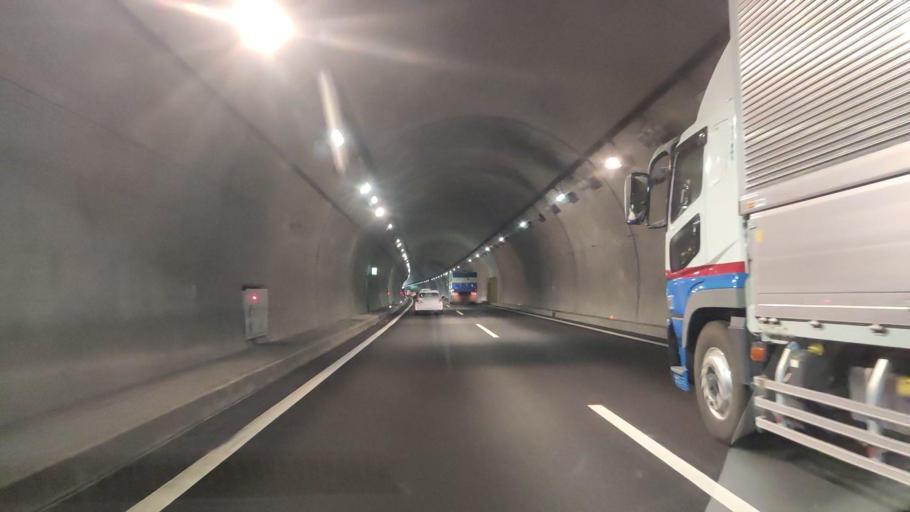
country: JP
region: Kanagawa
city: Zama
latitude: 35.5139
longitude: 139.3613
